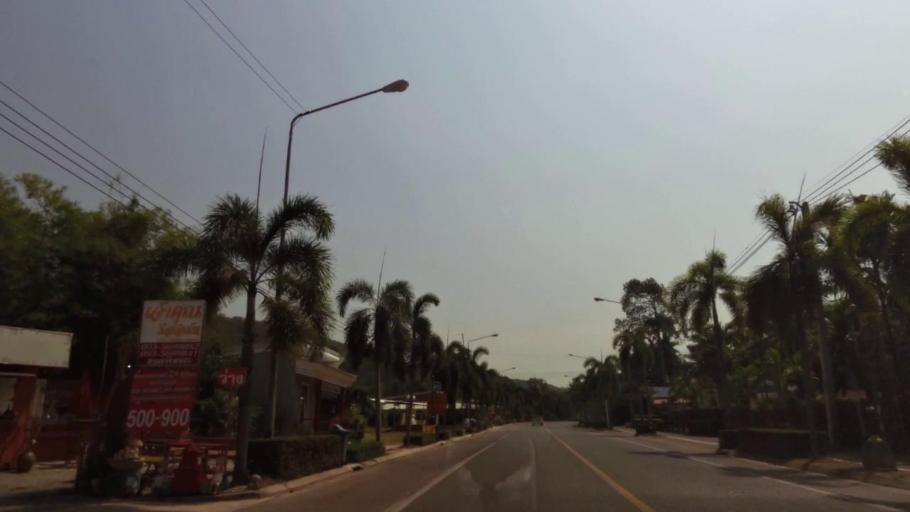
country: TH
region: Chanthaburi
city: Tha Mai
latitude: 12.5355
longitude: 101.9410
